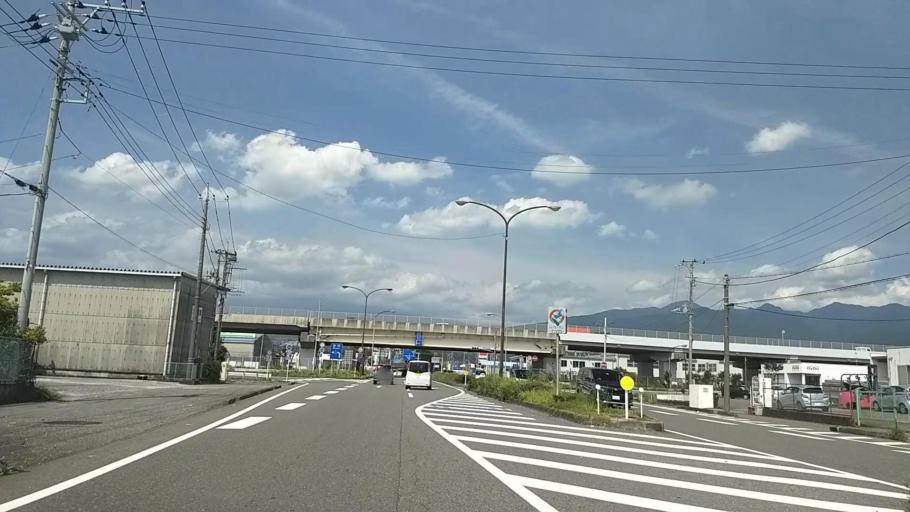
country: JP
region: Shizuoka
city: Fuji
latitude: 35.1479
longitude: 138.7133
